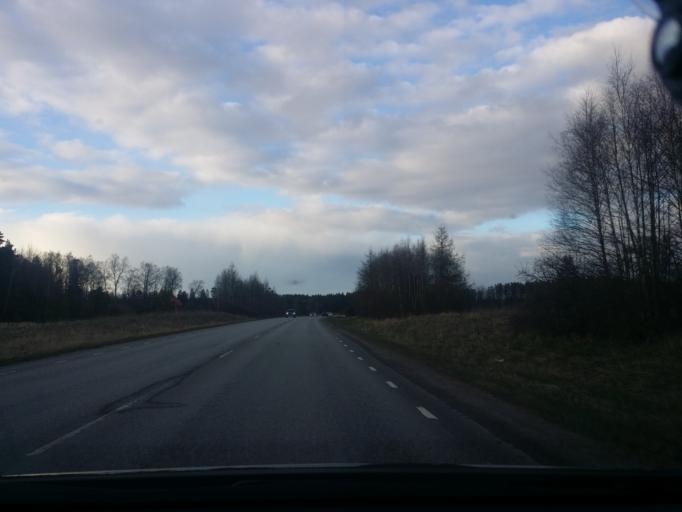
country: SE
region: Vaestmanland
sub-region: Vasteras
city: Vasteras
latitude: 59.6260
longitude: 16.4634
